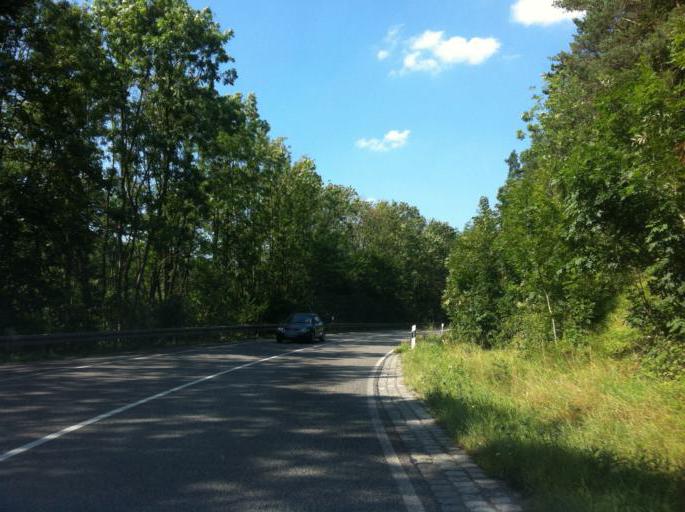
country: DE
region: Thuringia
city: Geisleden
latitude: 51.3581
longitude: 10.1785
